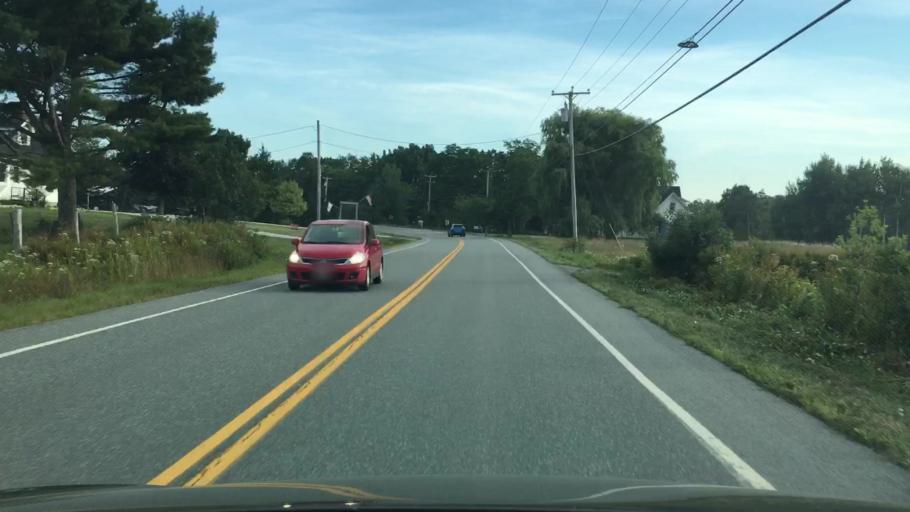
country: US
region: Maine
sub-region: Hancock County
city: Penobscot
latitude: 44.4636
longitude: -68.7827
